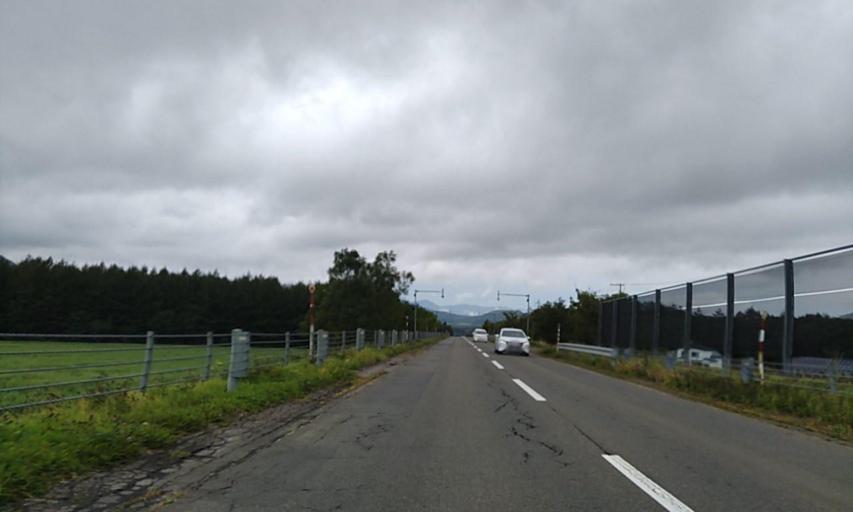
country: JP
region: Hokkaido
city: Bihoro
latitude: 43.5133
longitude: 144.4402
